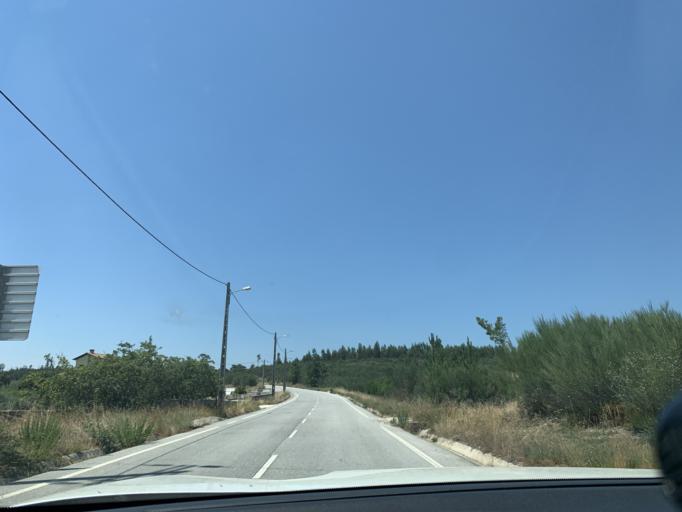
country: PT
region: Viseu
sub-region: Mangualde
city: Mangualde
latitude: 40.5485
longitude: -7.7414
